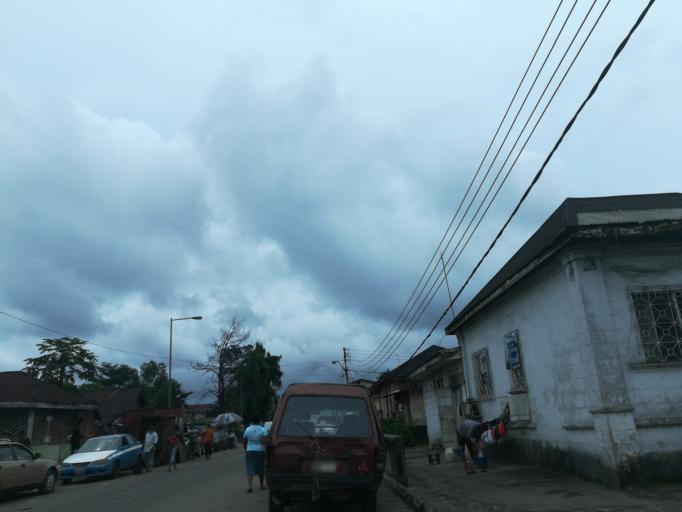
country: NG
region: Rivers
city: Port Harcourt
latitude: 4.7611
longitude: 7.0279
